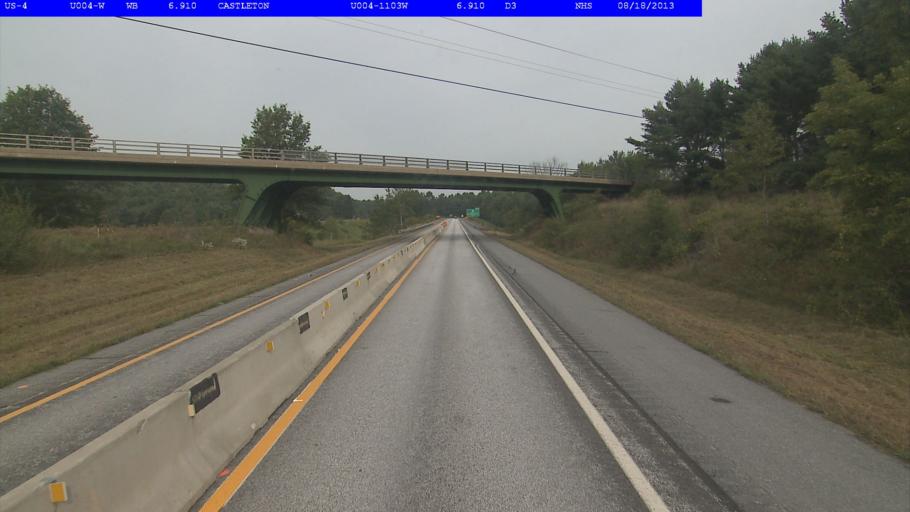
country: US
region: Vermont
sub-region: Rutland County
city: Castleton
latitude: 43.6195
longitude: -73.1813
